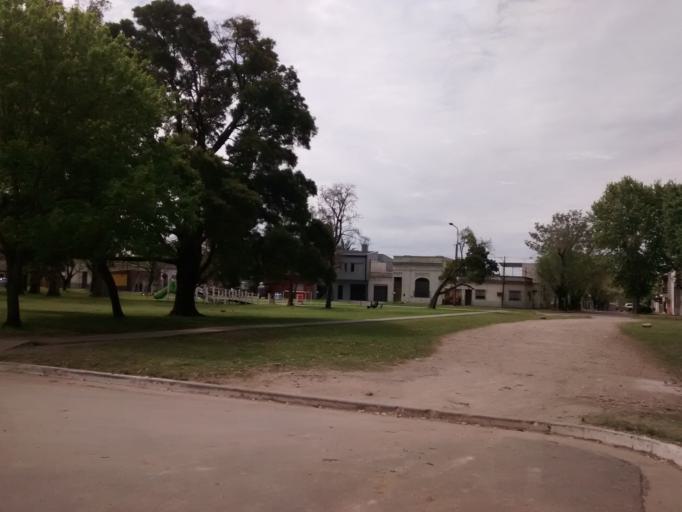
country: AR
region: Buenos Aires
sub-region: Partido de La Plata
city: La Plata
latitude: -34.8920
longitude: -57.9533
